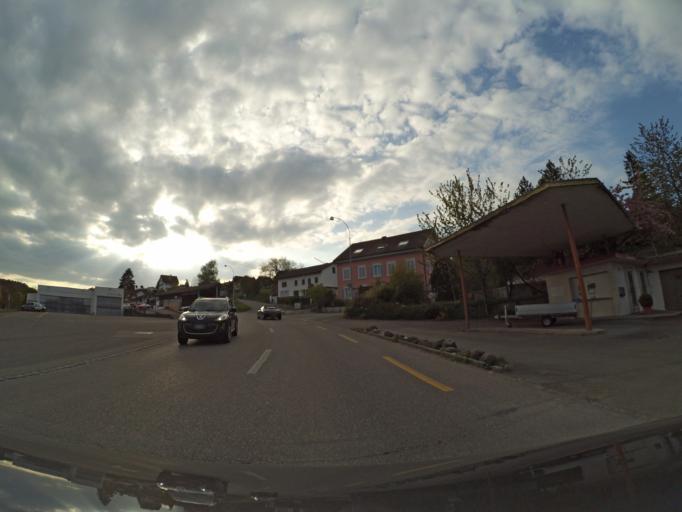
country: CH
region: Schaffhausen
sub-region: Bezirk Schleitheim
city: Schleitheim
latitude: 47.7474
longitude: 8.4796
